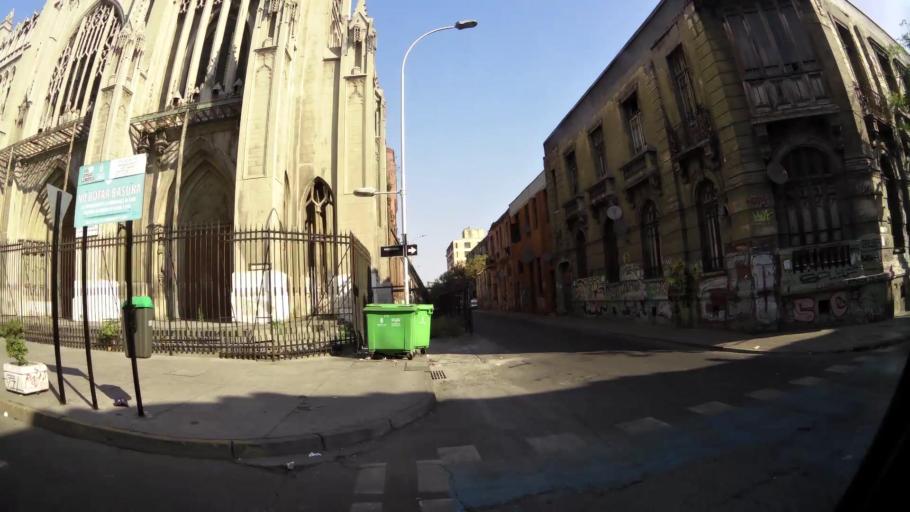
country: CL
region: Santiago Metropolitan
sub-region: Provincia de Santiago
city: Santiago
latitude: -33.4408
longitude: -70.6622
